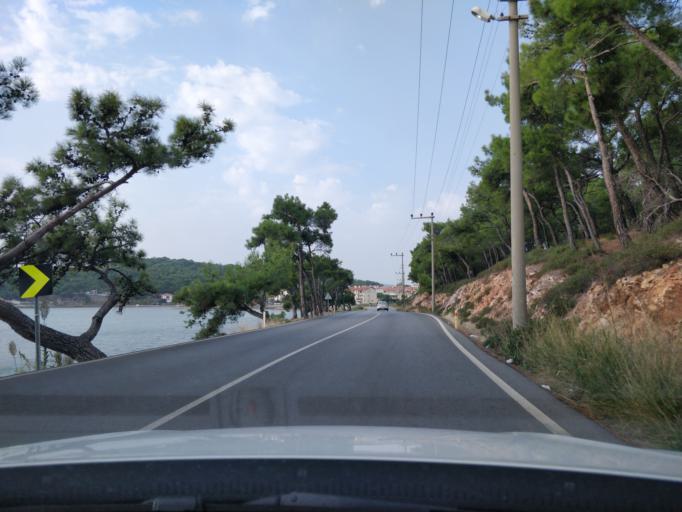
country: TR
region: Balikesir
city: Ayvalik
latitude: 39.2934
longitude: 26.6676
